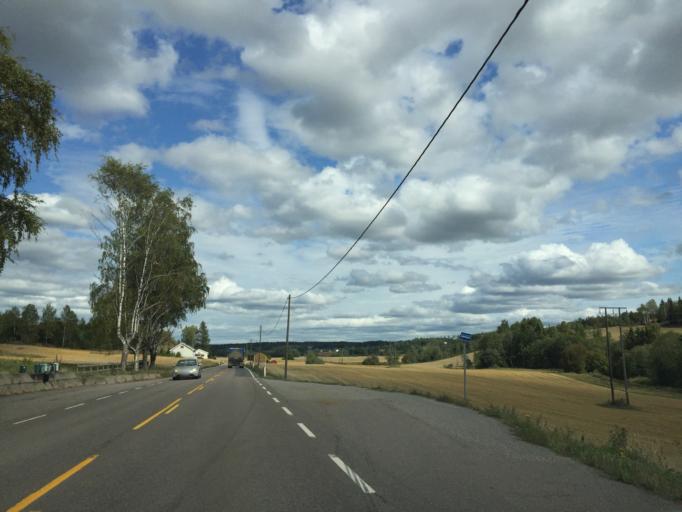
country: NO
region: Ostfold
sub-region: Hobol
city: Elvestad
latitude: 59.6110
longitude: 10.9271
